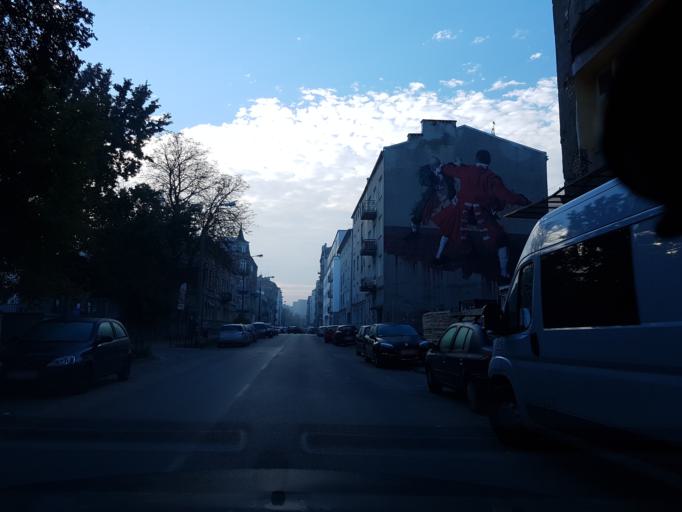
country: PL
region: Masovian Voivodeship
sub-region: Warszawa
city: Praga Polnoc
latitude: 52.2620
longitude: 21.0388
